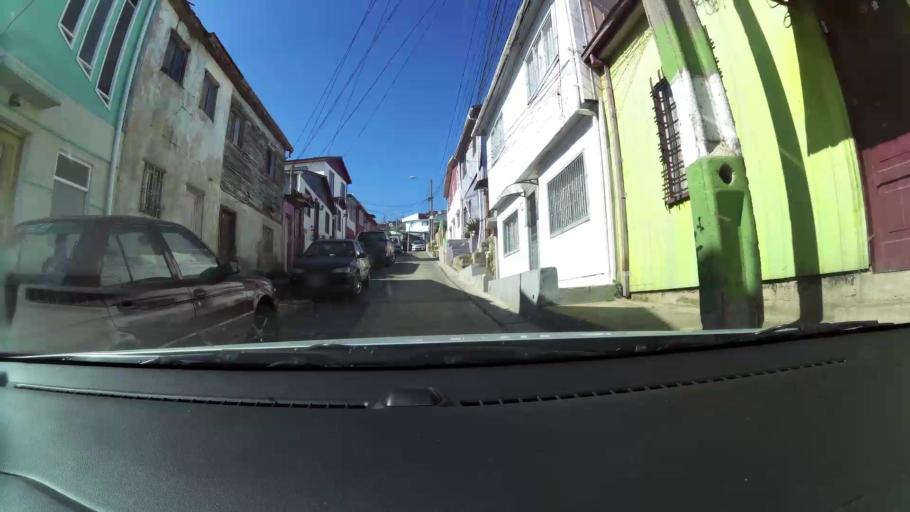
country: CL
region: Valparaiso
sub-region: Provincia de Valparaiso
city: Valparaiso
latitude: -33.0437
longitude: -71.6399
